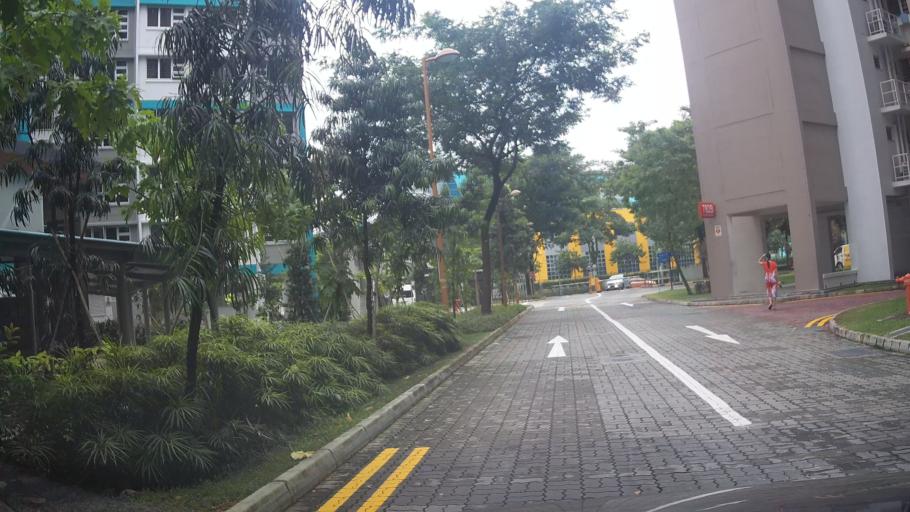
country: MY
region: Johor
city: Johor Bahru
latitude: 1.4475
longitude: 103.8035
